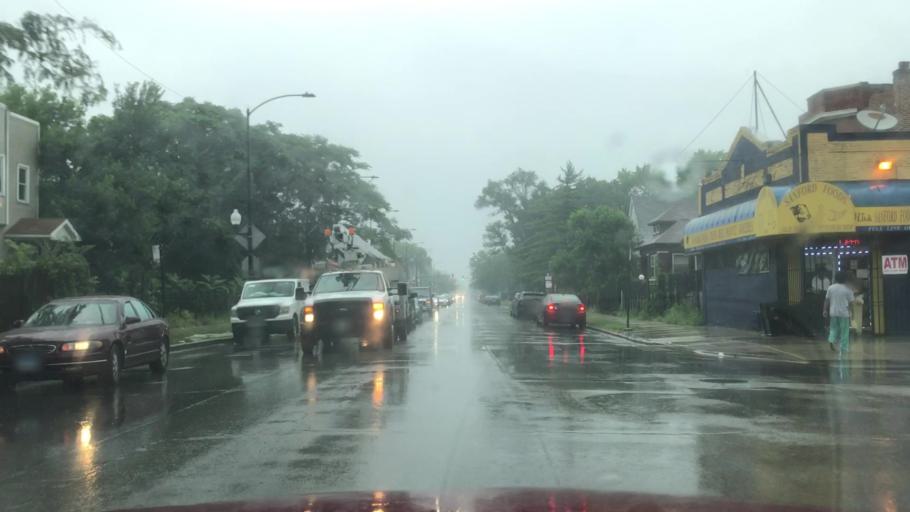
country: US
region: Illinois
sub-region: Cook County
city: Oak Park
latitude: 41.8892
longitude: -87.7554
